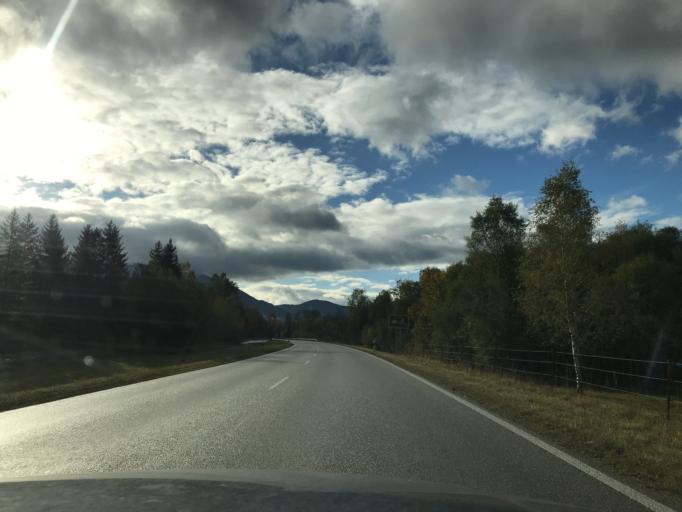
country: DE
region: Bavaria
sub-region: Upper Bavaria
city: Lenggries
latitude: 47.6915
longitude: 11.5662
